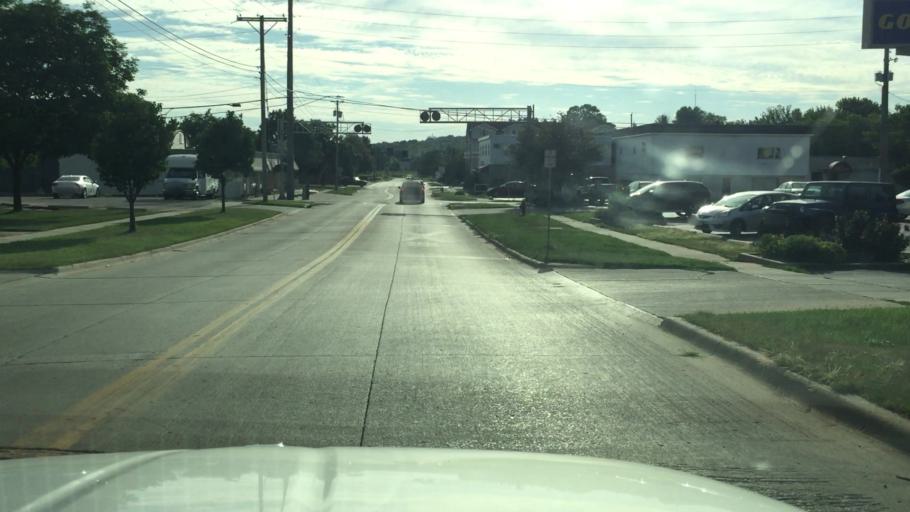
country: US
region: Iowa
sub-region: Johnson County
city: Iowa City
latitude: 41.6495
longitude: -91.5299
